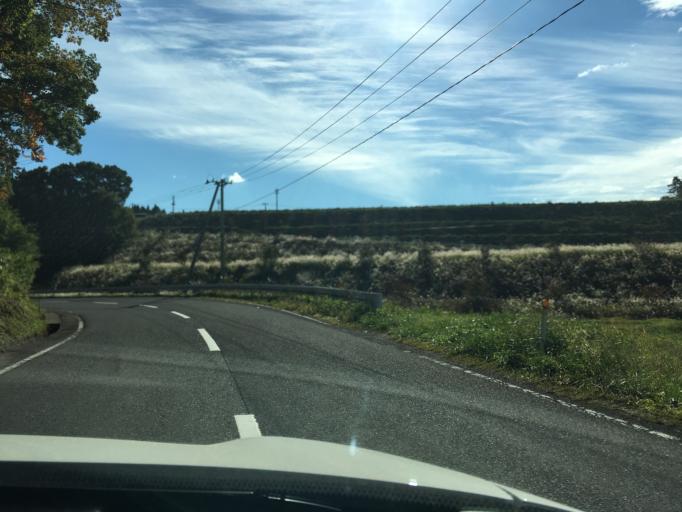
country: JP
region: Fukushima
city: Ishikawa
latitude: 37.1850
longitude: 140.5855
